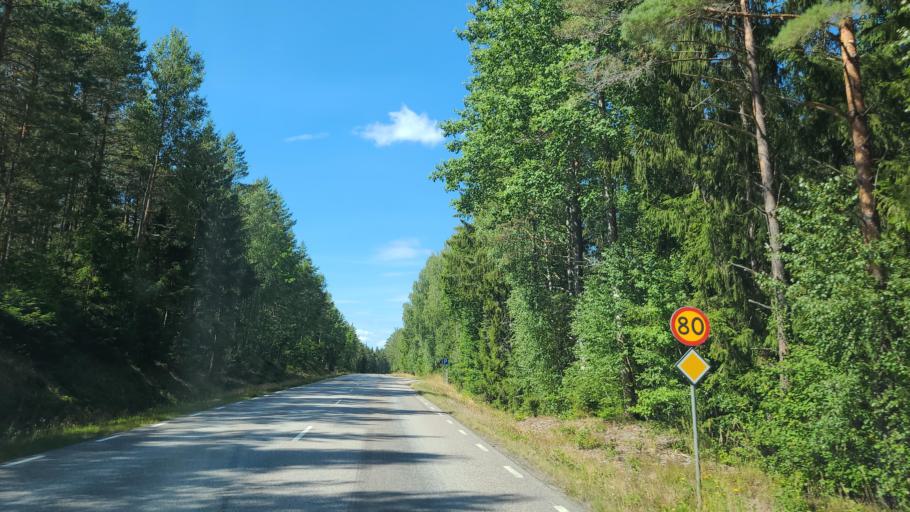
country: SE
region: Kalmar
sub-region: Nybro Kommun
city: Nybro
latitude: 56.5642
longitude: 15.8258
